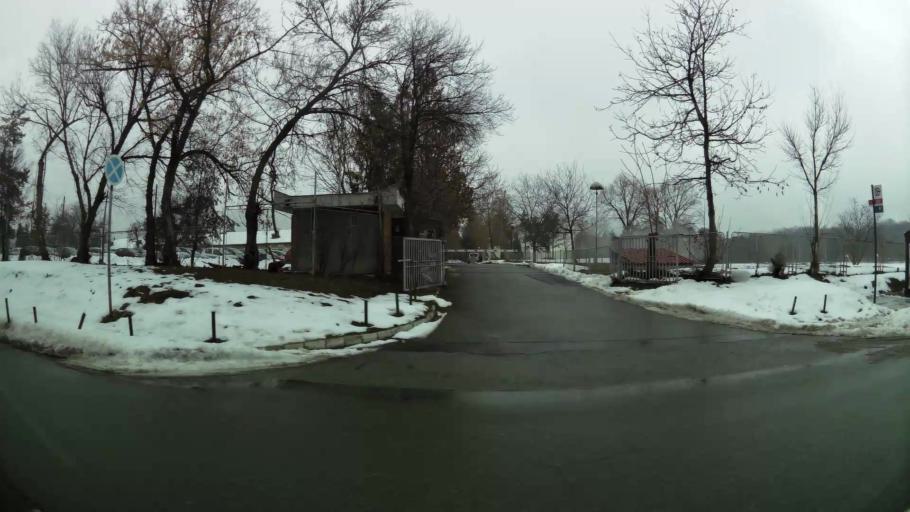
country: RS
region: Central Serbia
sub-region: Belgrade
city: Savski Venac
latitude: 44.7675
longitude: 20.4619
